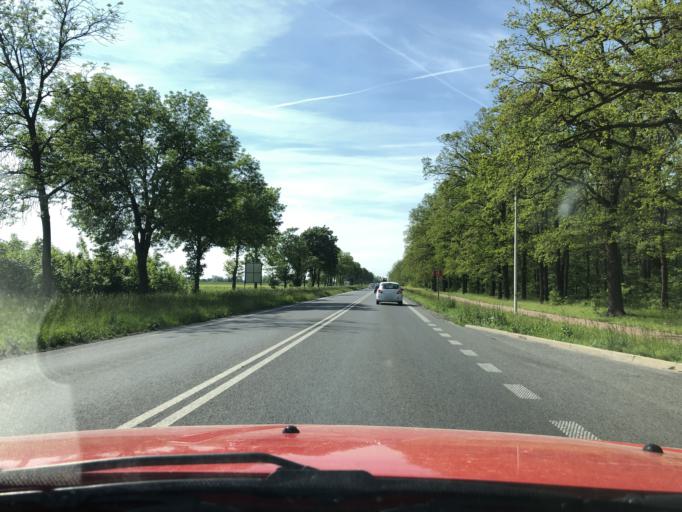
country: PL
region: Greater Poland Voivodeship
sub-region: Powiat pleszewski
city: Goluchow
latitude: 51.8553
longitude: 17.9210
